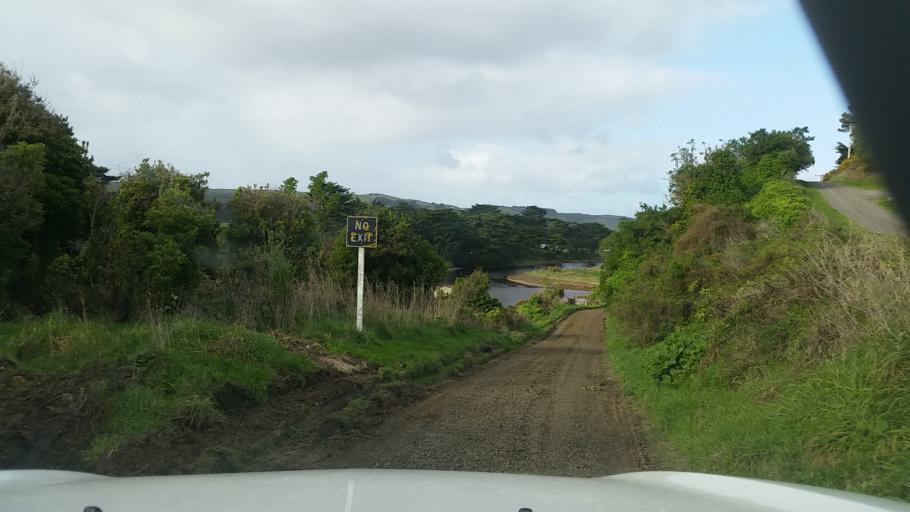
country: NZ
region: Chatham Islands
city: Waitangi
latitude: -43.9542
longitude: -176.5583
